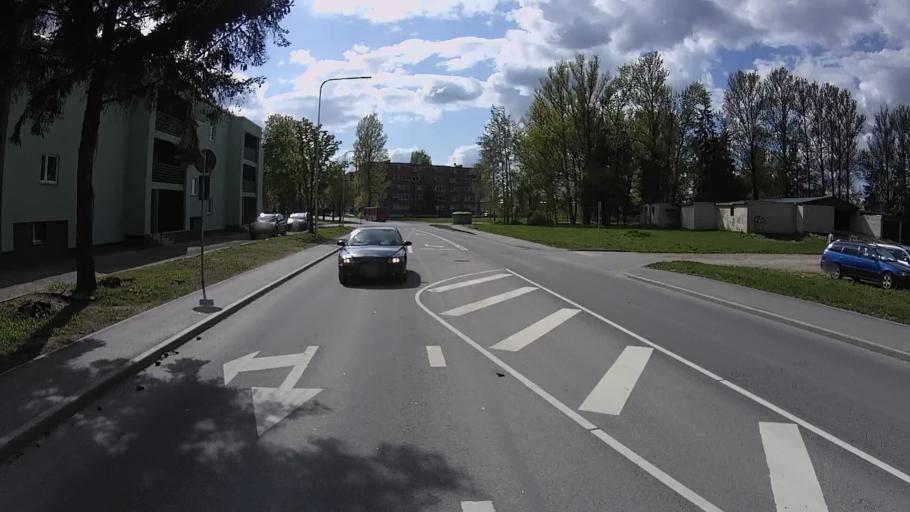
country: EE
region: Tartu
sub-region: Tartu linn
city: Tartu
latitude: 58.4007
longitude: 26.7170
